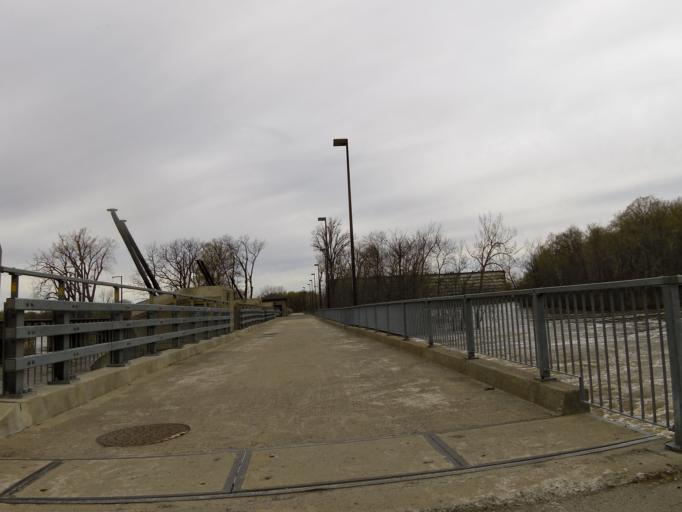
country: CA
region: Quebec
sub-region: Laurentides
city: Deux-Montagnes
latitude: 45.5322
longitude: -73.8812
